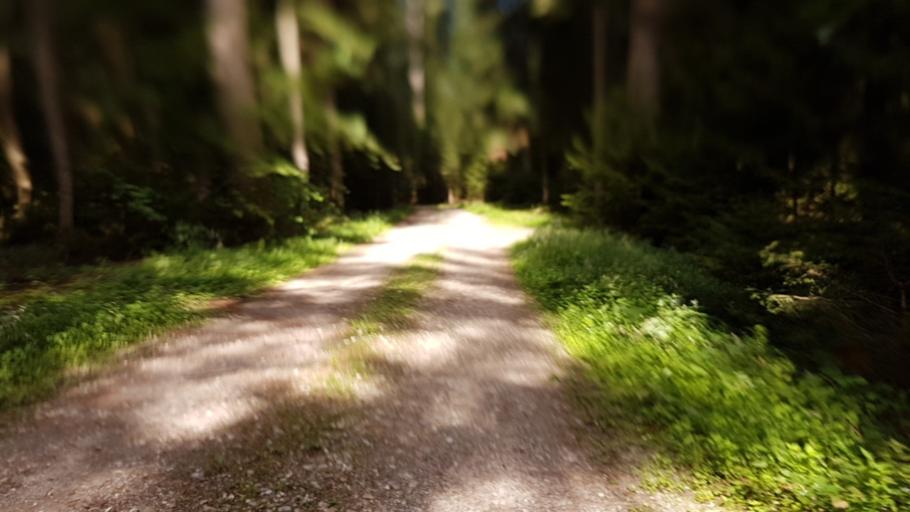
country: CH
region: Bern
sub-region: Bern-Mittelland District
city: Bowil
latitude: 46.8495
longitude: 7.7315
